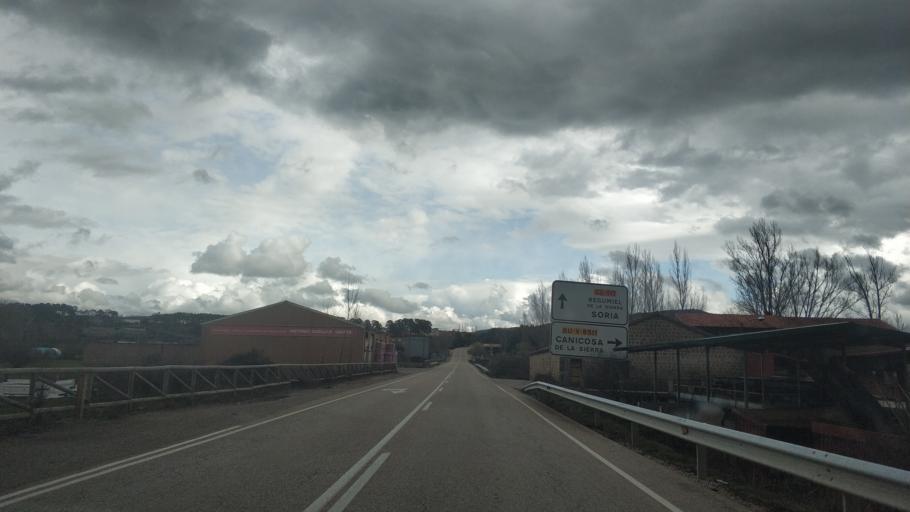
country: ES
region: Castille and Leon
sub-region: Provincia de Burgos
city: Quintanar de la Sierra
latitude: 41.9750
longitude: -3.0453
